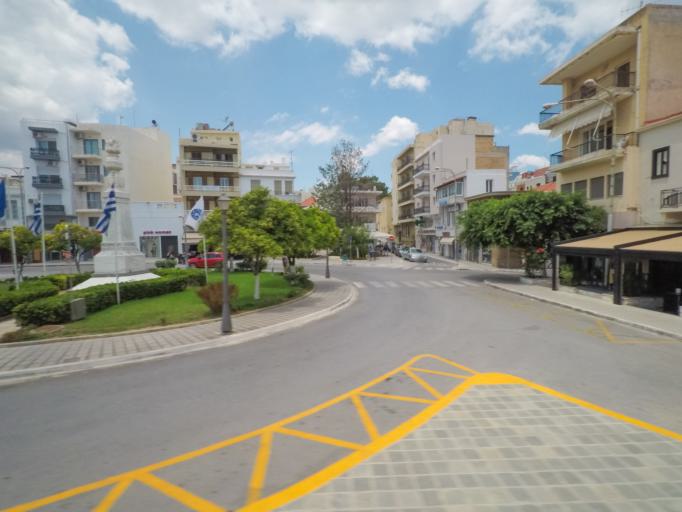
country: GR
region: Crete
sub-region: Nomos Lasithiou
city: Agios Nikolaos
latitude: 35.1891
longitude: 25.7173
